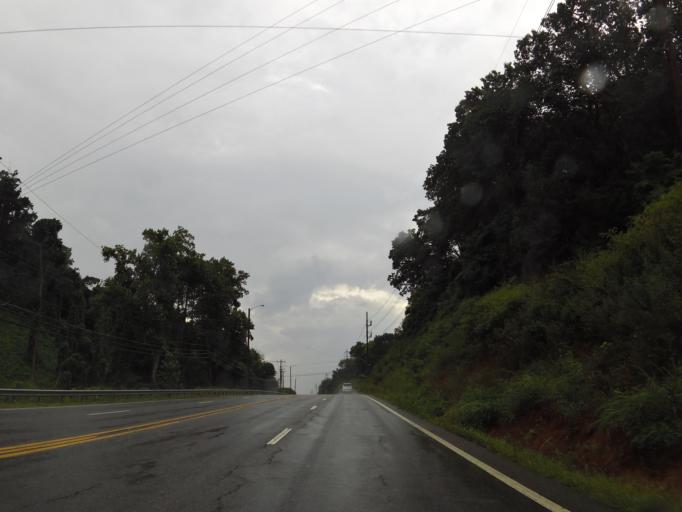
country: US
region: Tennessee
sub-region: Knox County
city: Knoxville
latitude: 35.9139
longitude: -83.8557
